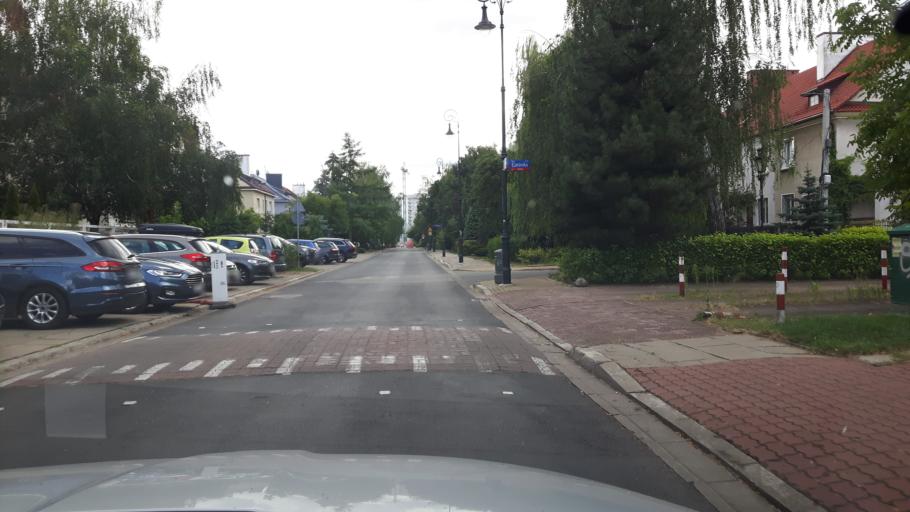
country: PL
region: Masovian Voivodeship
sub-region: Warszawa
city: Wilanow
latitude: 52.1800
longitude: 21.0624
